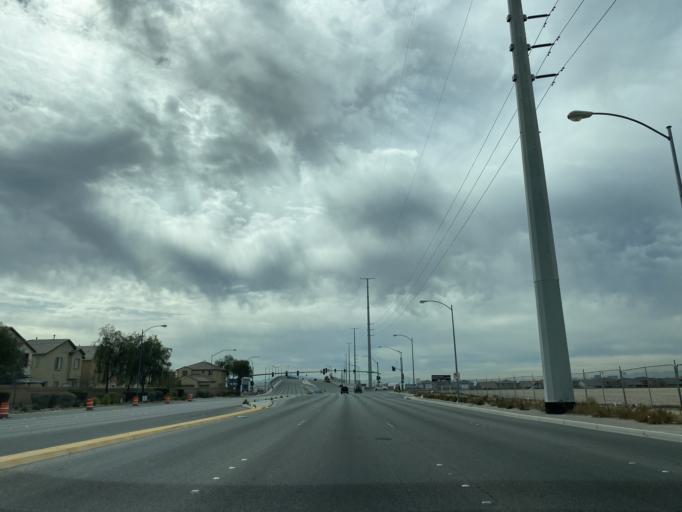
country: US
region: Nevada
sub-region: Clark County
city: Nellis Air Force Base
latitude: 36.2711
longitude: -115.0800
